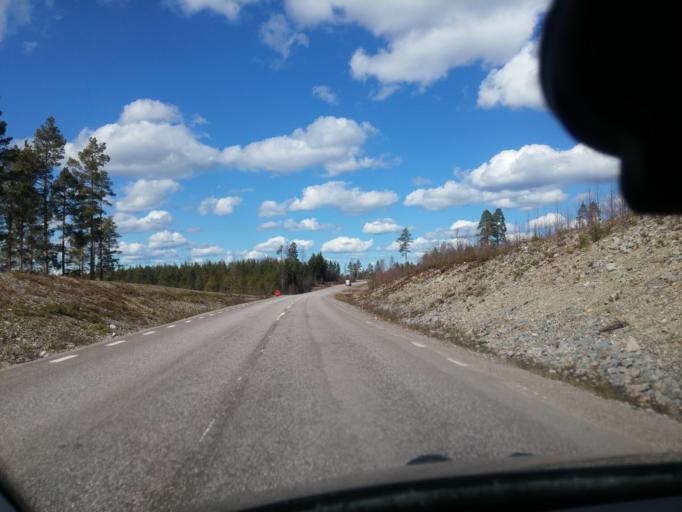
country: SE
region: Gaevleborg
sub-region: Ovanakers Kommun
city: Edsbyn
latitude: 61.2346
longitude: 15.8820
